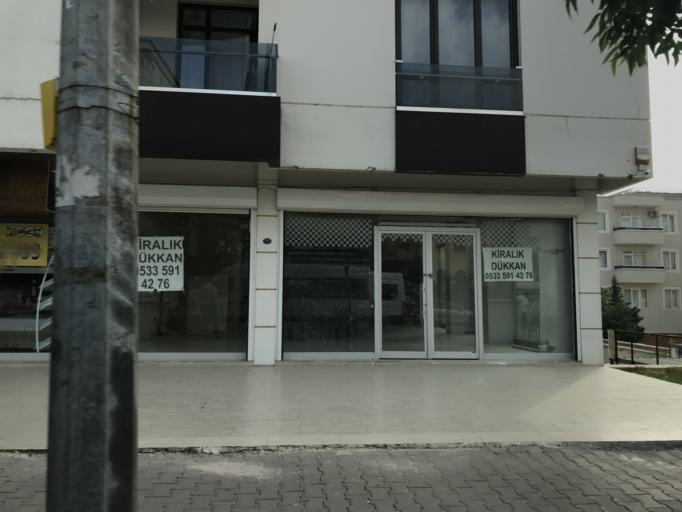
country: TR
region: Gaziantep
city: Sahinbey
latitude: 37.0554
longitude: 37.3320
